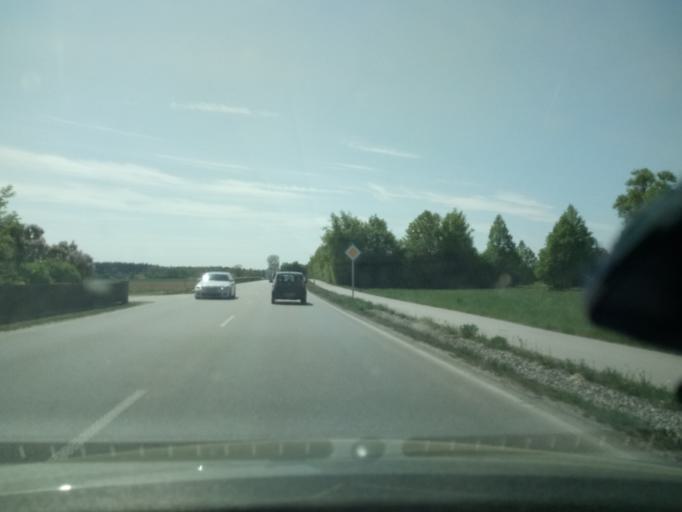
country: DE
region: Bavaria
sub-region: Upper Bavaria
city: Ampfing
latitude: 48.2432
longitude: 12.4122
